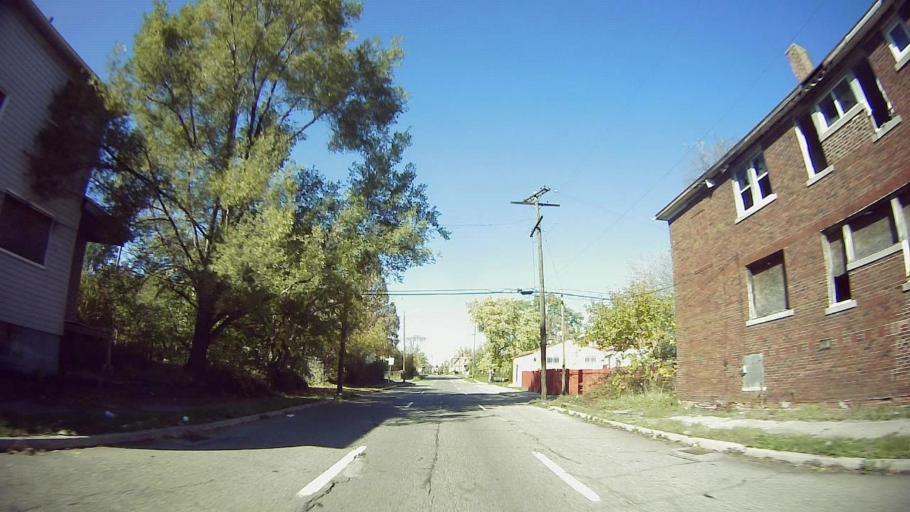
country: US
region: Michigan
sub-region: Wayne County
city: Highland Park
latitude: 42.3878
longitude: -83.1102
